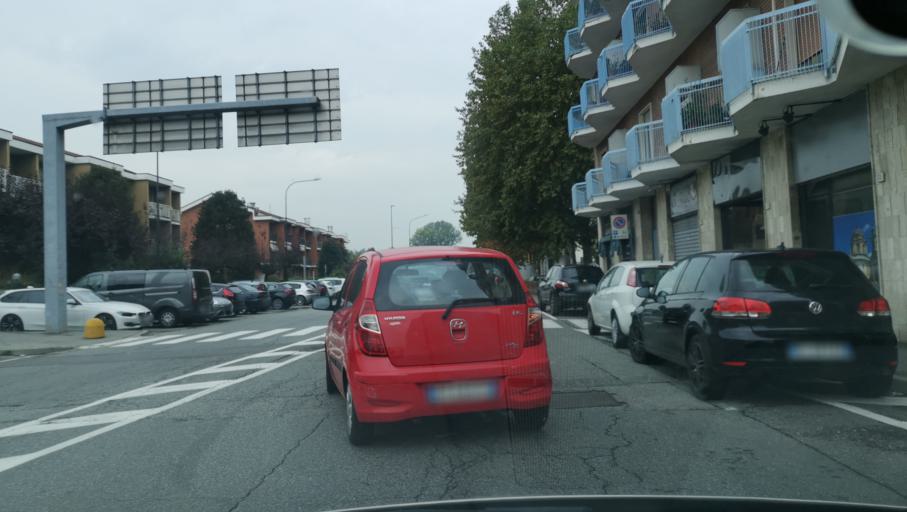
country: IT
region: Piedmont
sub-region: Provincia di Torino
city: Settimo Torinese
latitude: 45.1294
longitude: 7.7546
